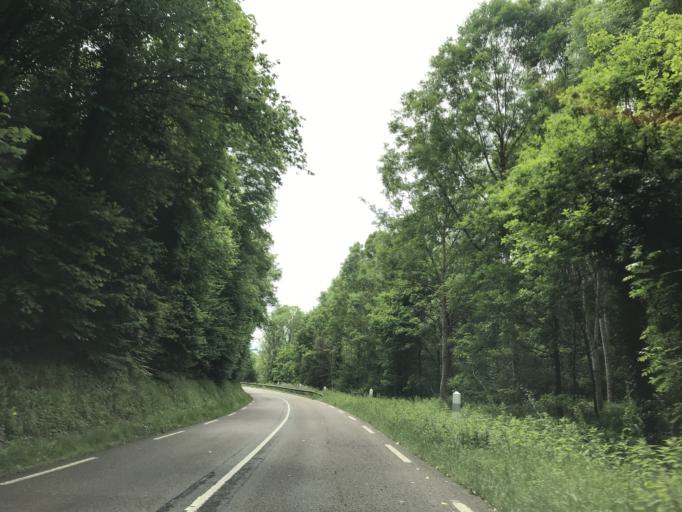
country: FR
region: Ile-de-France
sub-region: Departement des Yvelines
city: Rosny-sur-Seine
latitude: 48.9922
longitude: 1.6173
